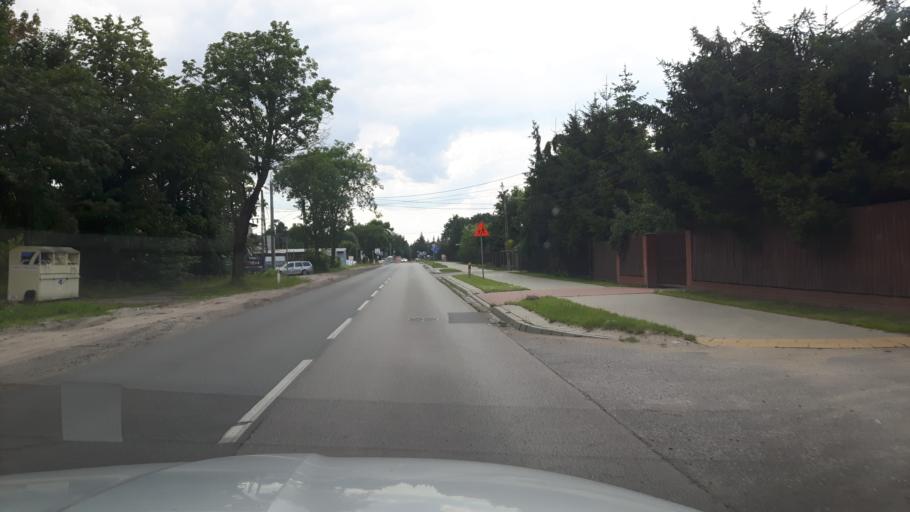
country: PL
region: Masovian Voivodeship
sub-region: Powiat wolominski
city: Duczki
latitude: 52.3633
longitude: 21.2934
